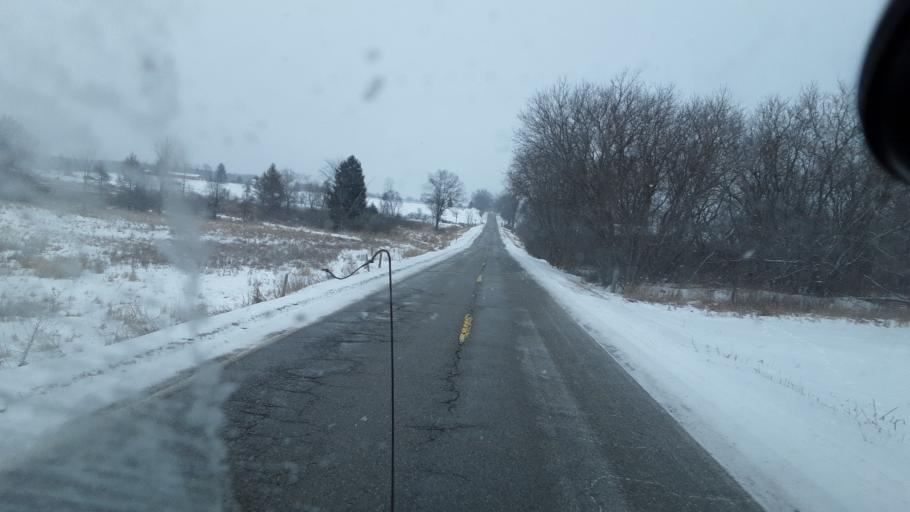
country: US
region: Michigan
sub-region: Ingham County
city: Leslie
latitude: 42.4896
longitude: -84.3403
